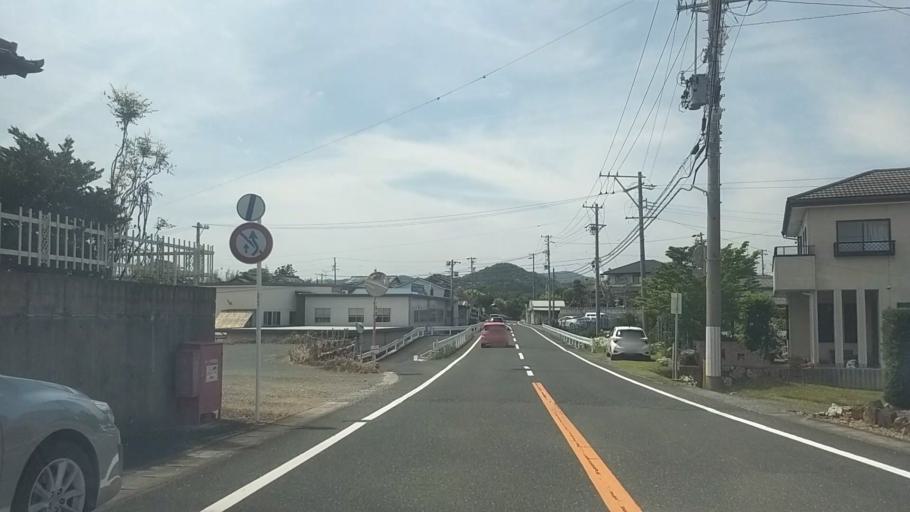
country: JP
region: Shizuoka
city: Kosai-shi
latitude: 34.7689
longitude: 137.5599
